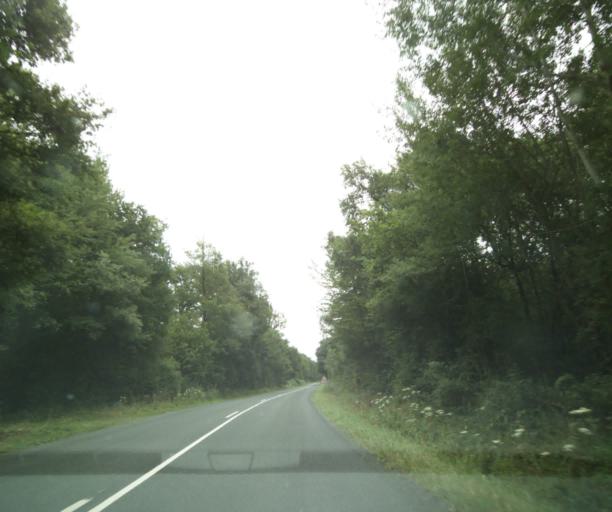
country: FR
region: Pays de la Loire
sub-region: Departement de la Sarthe
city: Precigne
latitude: 47.7468
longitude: -0.2889
